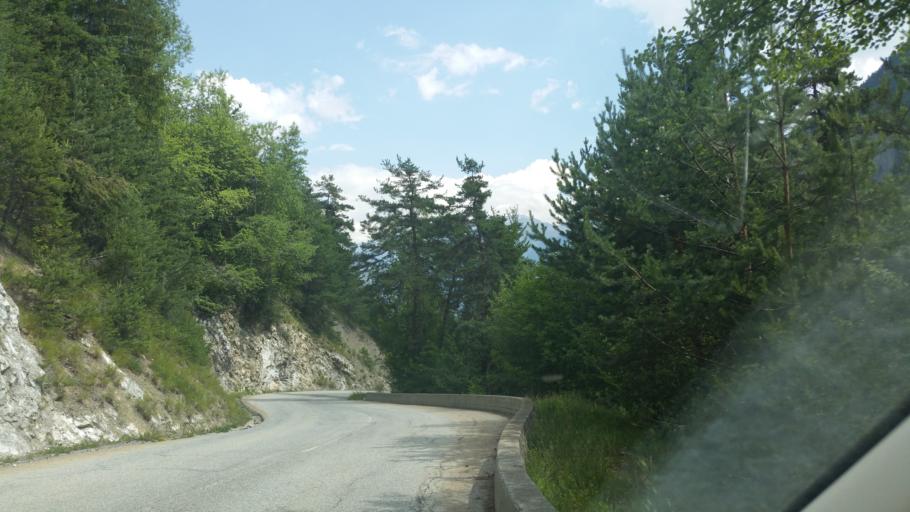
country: FR
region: Rhone-Alpes
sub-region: Departement de la Savoie
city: Saint-Jean-de-Maurienne
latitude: 45.2321
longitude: 6.3111
